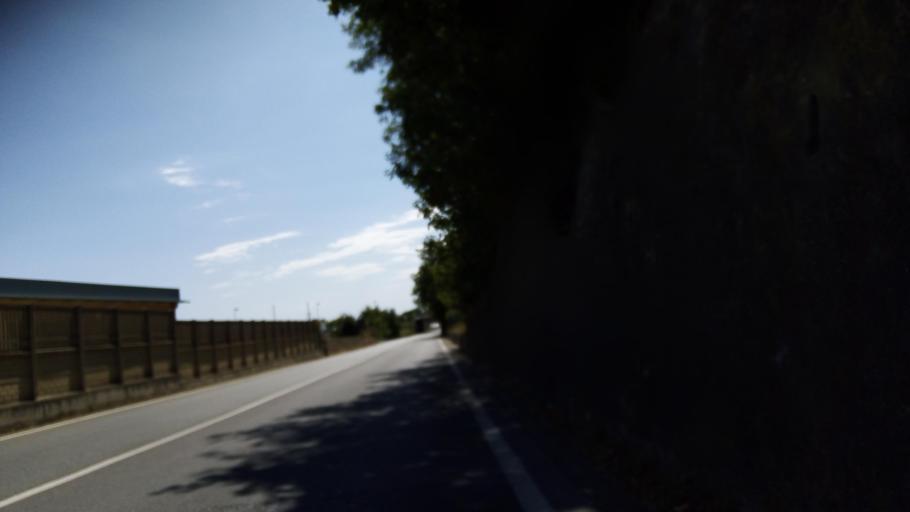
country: IT
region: Liguria
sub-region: Provincia di Savona
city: Boissano
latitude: 44.1187
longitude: 8.2237
